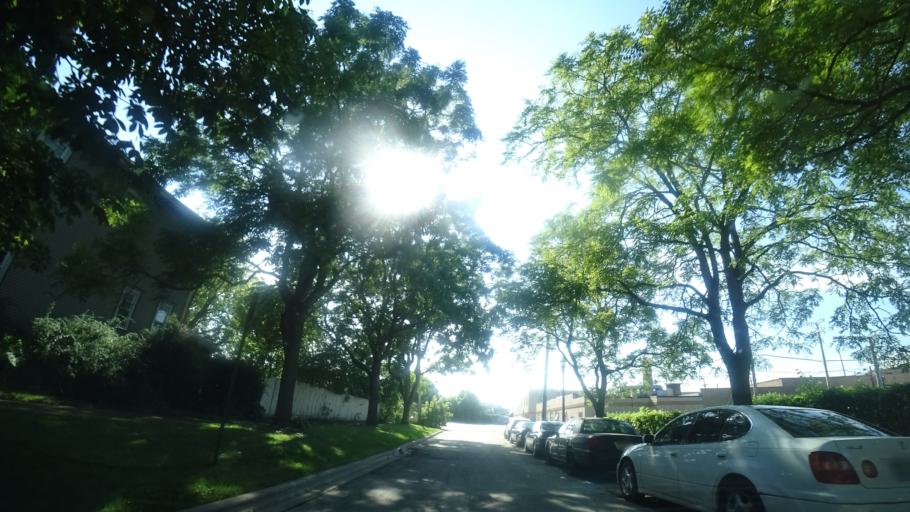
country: US
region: Illinois
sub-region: Cook County
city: Evanston
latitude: 42.0503
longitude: -87.6936
